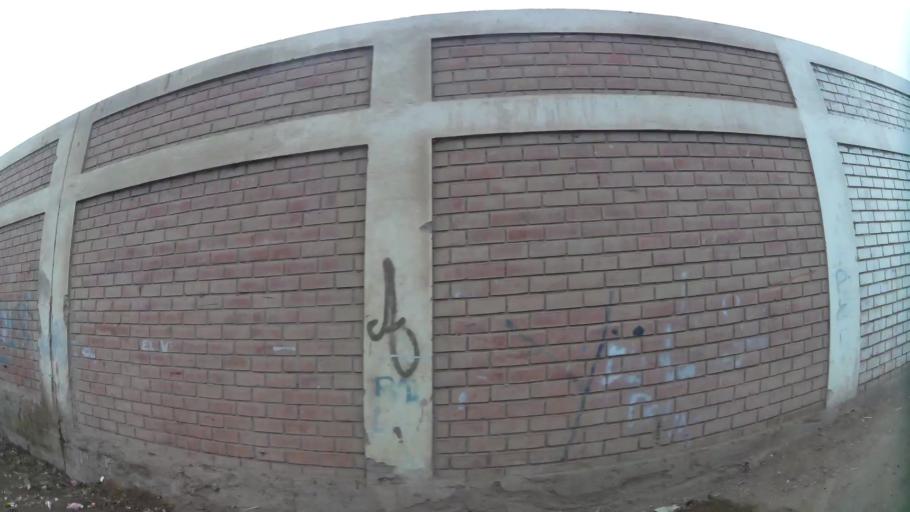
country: PE
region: Ica
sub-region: Provincia de Pisco
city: Pisco
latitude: -13.7086
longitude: -76.1974
